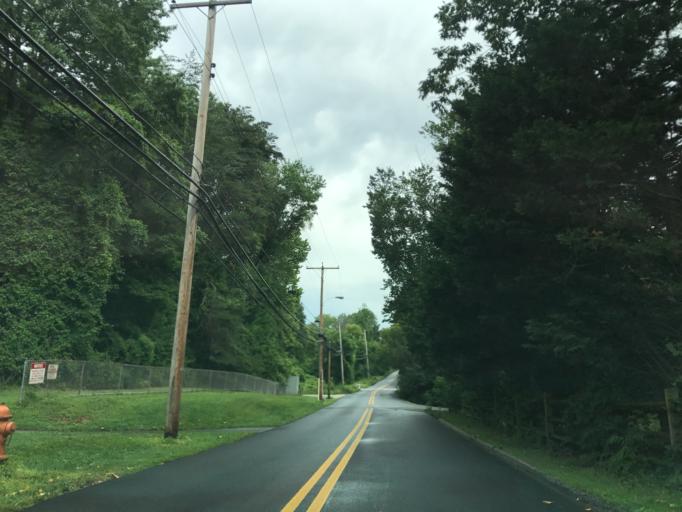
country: US
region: Maryland
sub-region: Baltimore County
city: Lutherville
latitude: 39.4032
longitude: -76.6351
